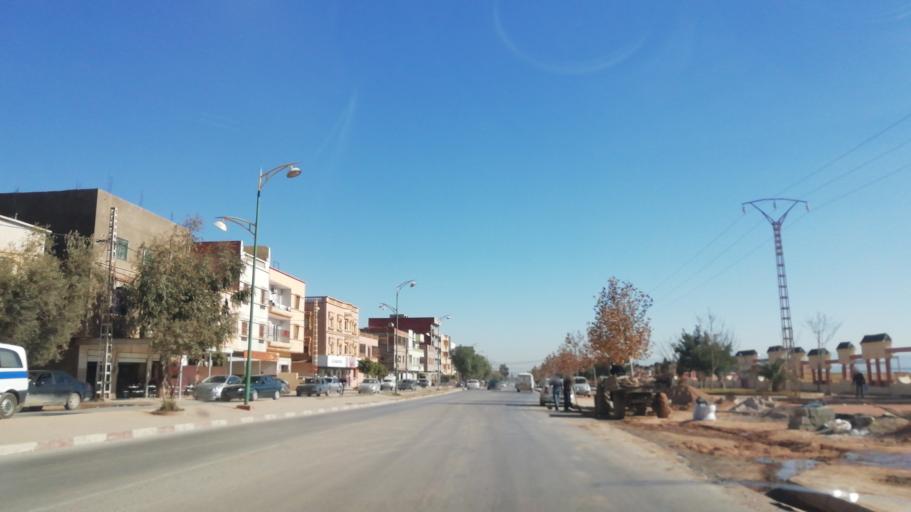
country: DZ
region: Tlemcen
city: Nedroma
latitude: 34.8444
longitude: -1.7556
